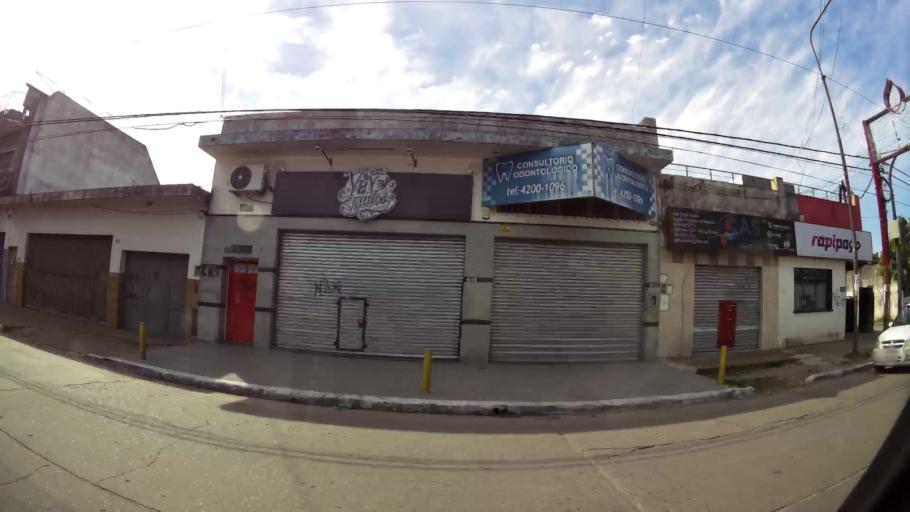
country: AR
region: Buenos Aires
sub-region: Partido de Quilmes
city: Quilmes
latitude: -34.7685
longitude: -58.2918
